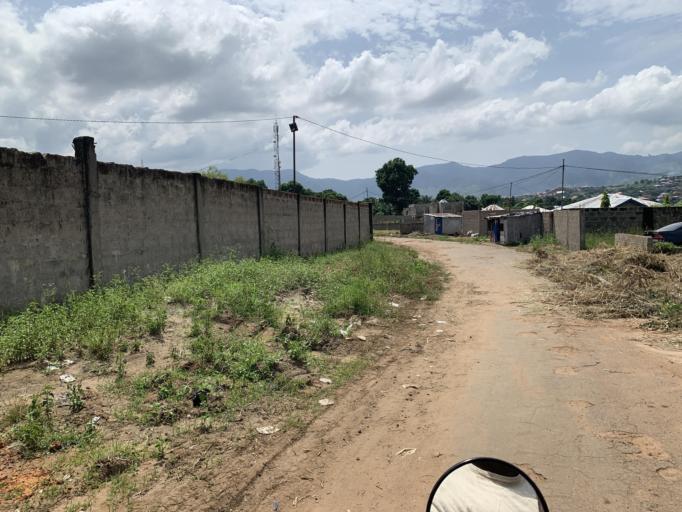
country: SL
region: Western Area
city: Hastings
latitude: 8.4124
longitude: -13.1312
